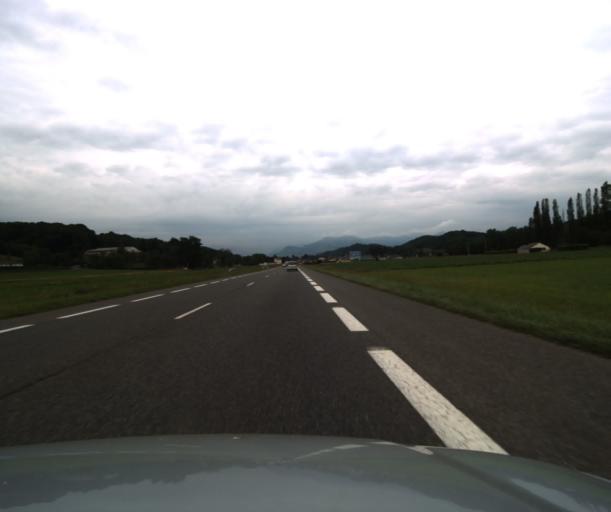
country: FR
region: Midi-Pyrenees
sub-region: Departement des Hautes-Pyrenees
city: Ossun
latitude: 43.1476
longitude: -0.0241
